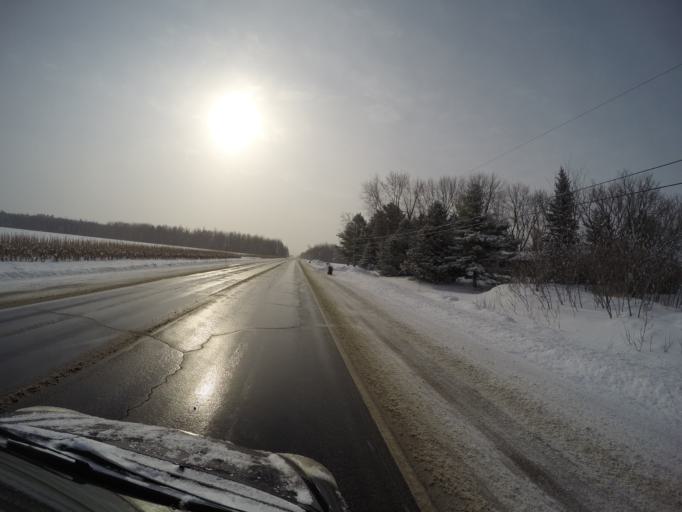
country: CA
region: Ontario
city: Clarence-Rockland
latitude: 45.4370
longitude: -75.4163
